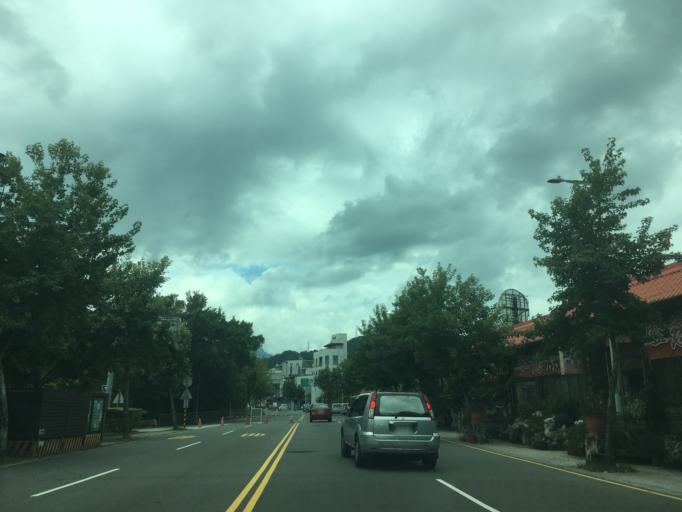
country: TW
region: Taiwan
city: Daxi
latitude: 24.8489
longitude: 121.2850
